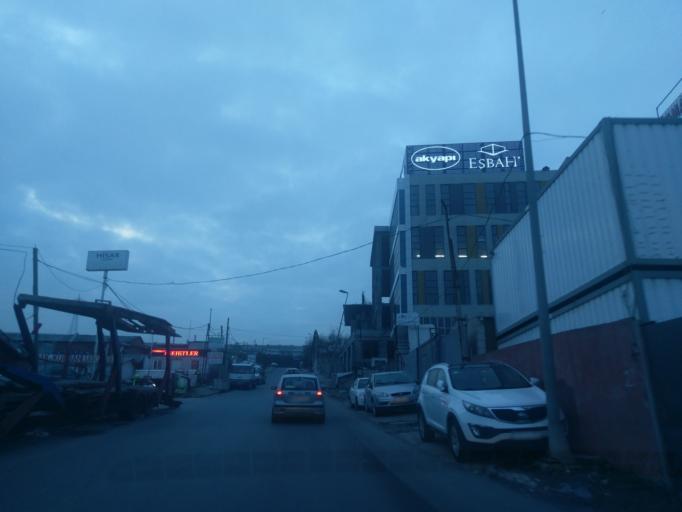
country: TR
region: Istanbul
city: Mahmutbey
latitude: 41.0674
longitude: 28.8130
